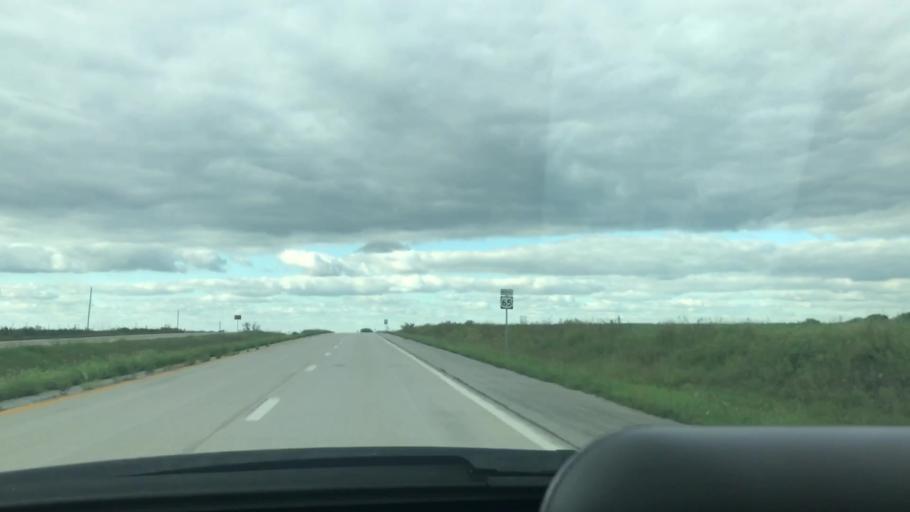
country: US
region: Missouri
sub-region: Benton County
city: Lincoln
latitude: 38.3550
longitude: -93.3397
